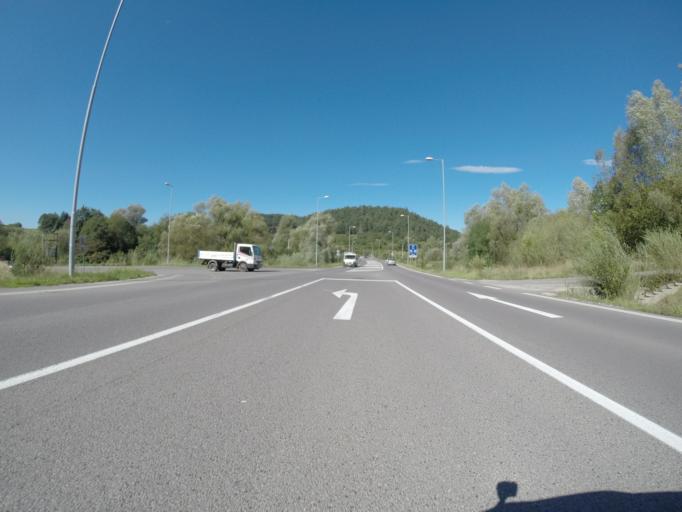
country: SK
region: Trenciansky
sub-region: Okres Povazska Bystrica
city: Povazska Bystrica
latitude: 49.1003
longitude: 18.4406
